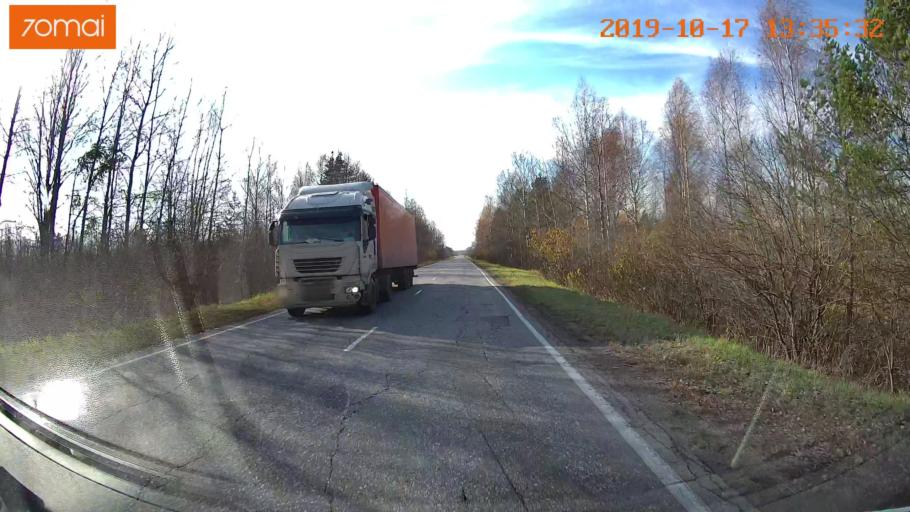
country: RU
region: Vladimir
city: Velikodvorskiy
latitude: 55.1420
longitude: 40.6872
